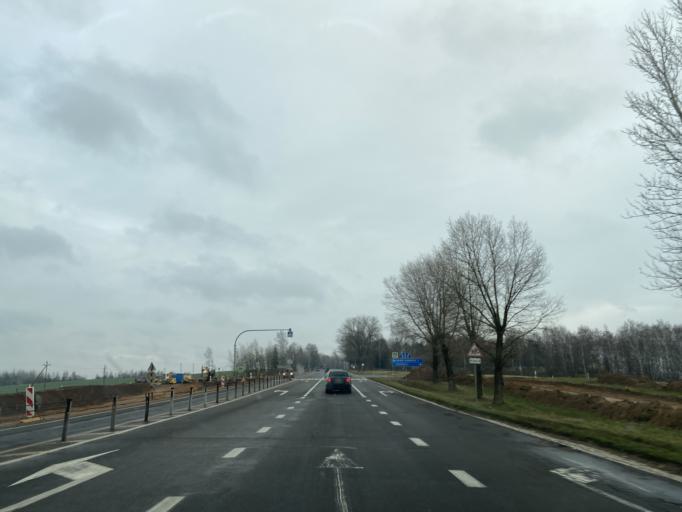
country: BY
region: Minsk
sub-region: Smalyavitski Rayon
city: Usjazh
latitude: 54.0288
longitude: 27.9744
